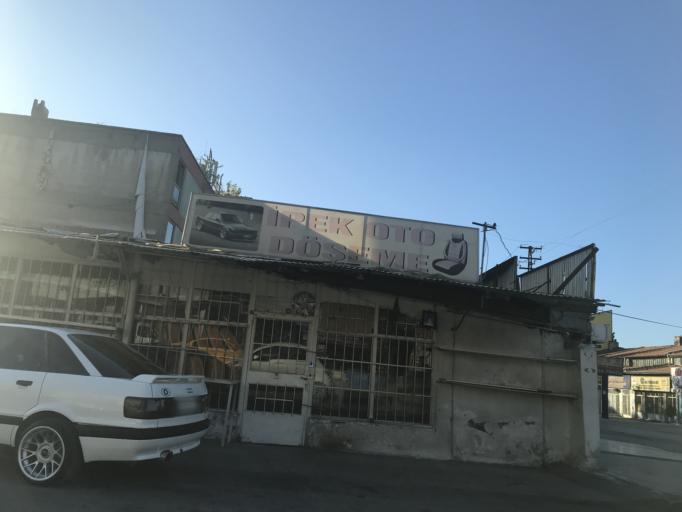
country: TR
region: Ankara
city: Ankara
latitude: 39.9477
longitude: 32.8429
